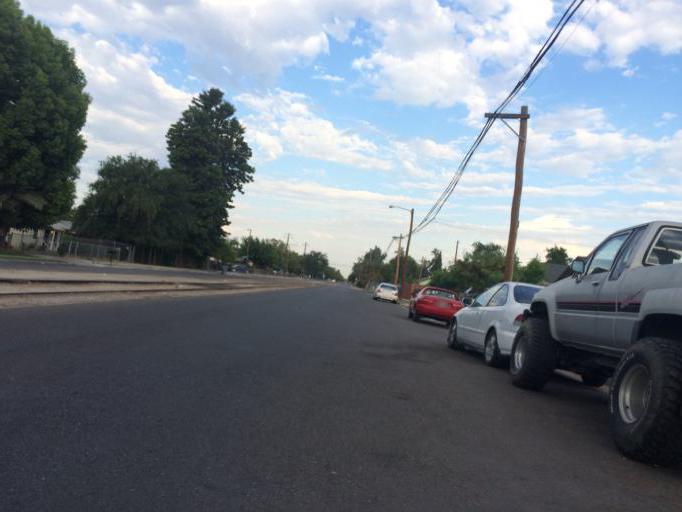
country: US
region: California
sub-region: Fresno County
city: Fresno
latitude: 36.7614
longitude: -119.7600
